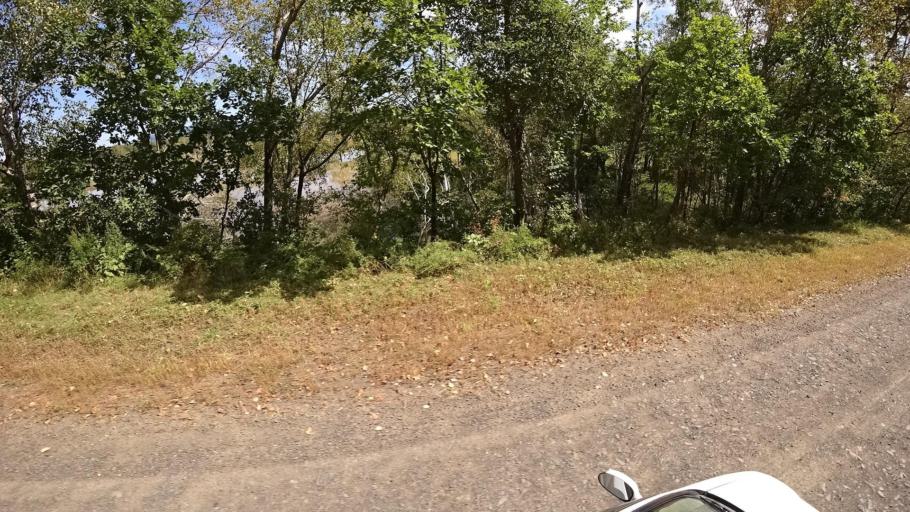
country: RU
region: Primorskiy
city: Yakovlevka
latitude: 44.6981
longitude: 133.6539
